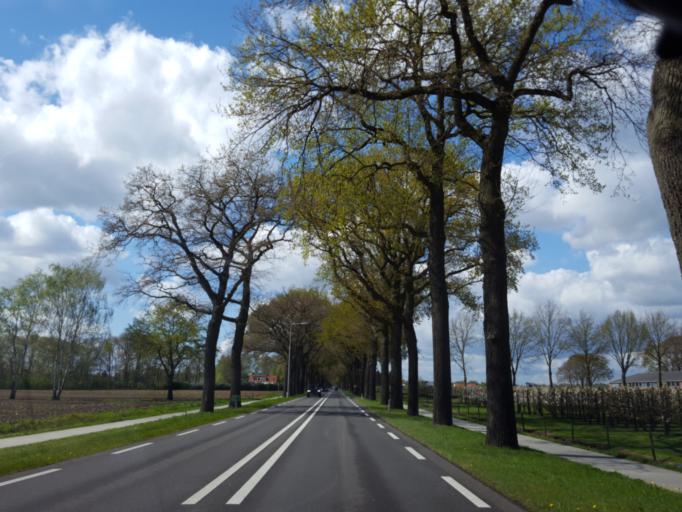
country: NL
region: Limburg
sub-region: Gemeente Nederweert
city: Nederweert
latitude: 51.2386
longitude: 5.7750
